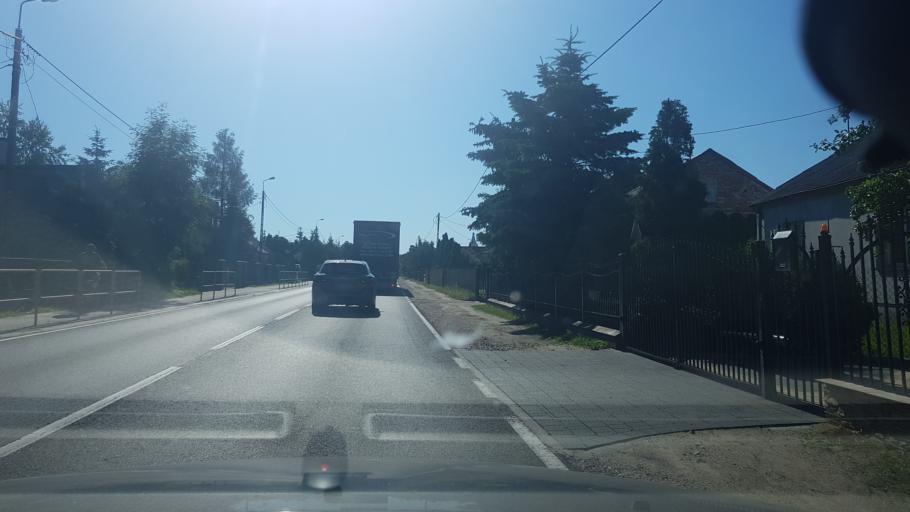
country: PL
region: Masovian Voivodeship
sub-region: Powiat wegrowski
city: Lochow
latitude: 52.5395
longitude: 21.6634
